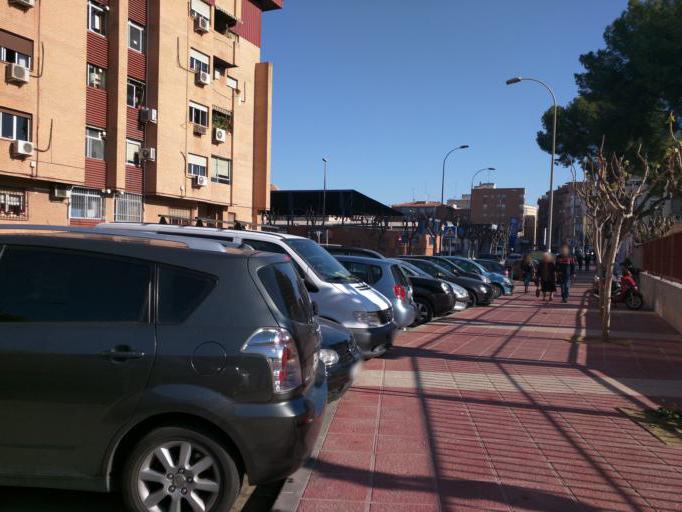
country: ES
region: Murcia
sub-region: Murcia
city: Murcia
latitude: 37.9848
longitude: -1.1407
